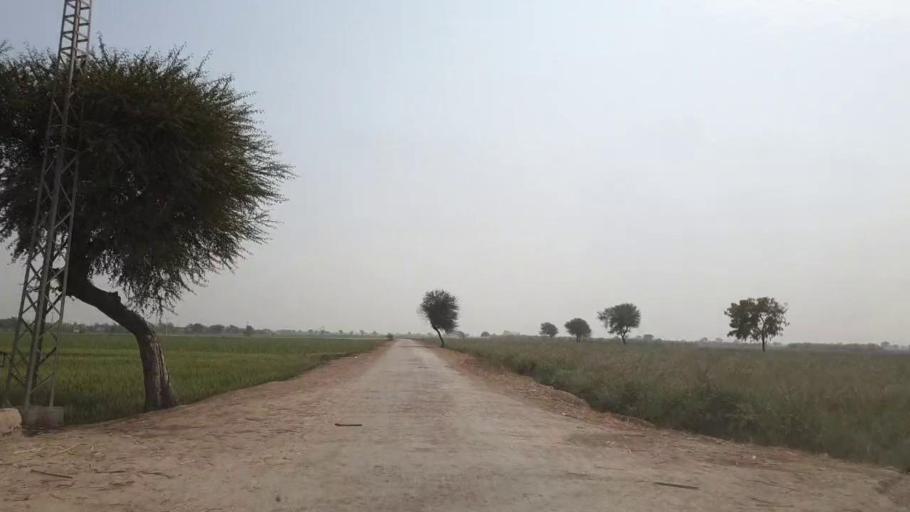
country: PK
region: Sindh
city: Mirpur Khas
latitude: 25.5401
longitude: 69.0870
